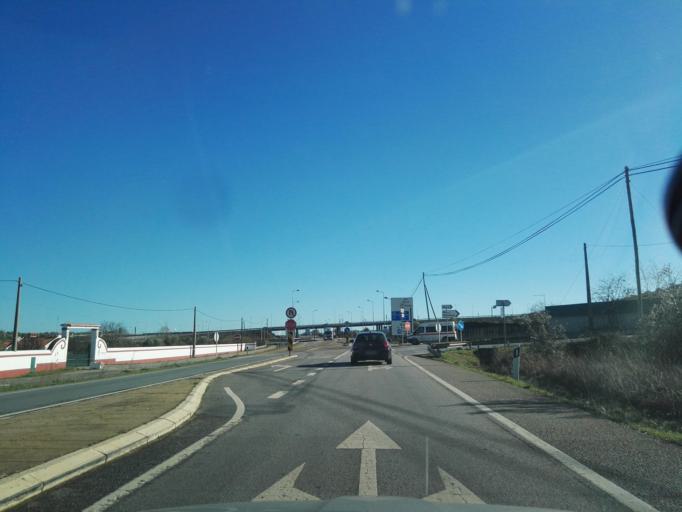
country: PT
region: Evora
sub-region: Borba
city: Borba
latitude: 38.8148
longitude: -7.4780
